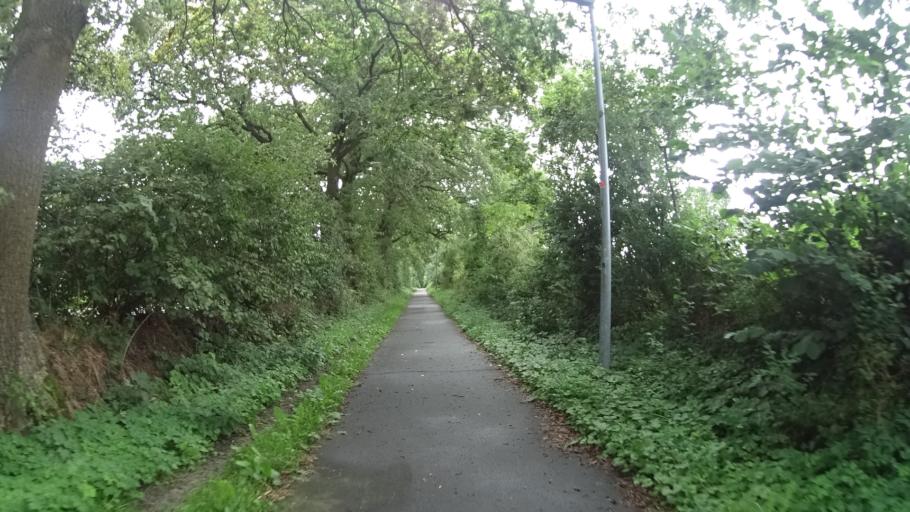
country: DE
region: Schleswig-Holstein
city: Tangstedt
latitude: 53.7401
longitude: 10.0716
